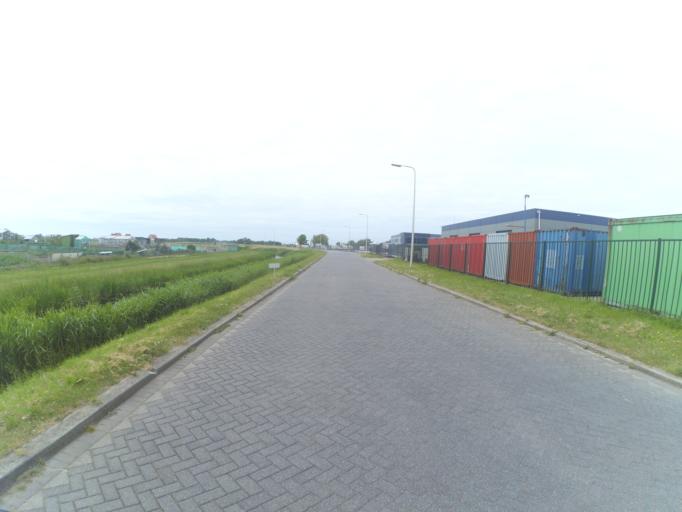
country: NL
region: South Holland
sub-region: Gemeente Spijkenisse
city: Spijkenisse
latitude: 51.8187
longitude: 4.2491
